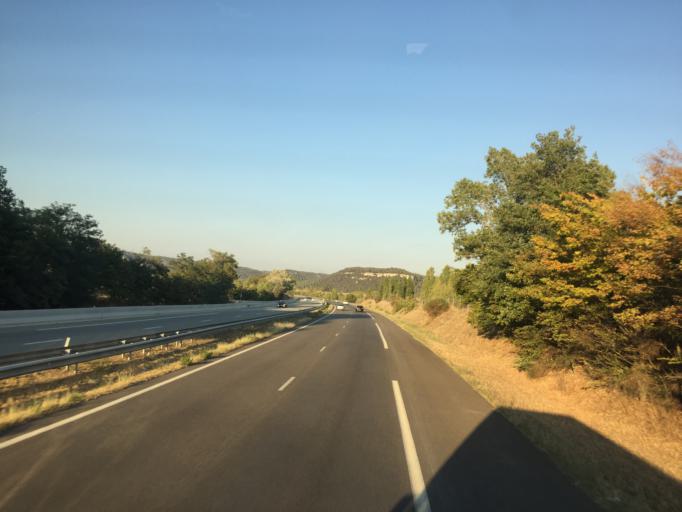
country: FR
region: Provence-Alpes-Cote d'Azur
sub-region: Departement des Bouches-du-Rhone
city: Peyrolles-en-Provence
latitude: 43.6561
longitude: 5.6111
